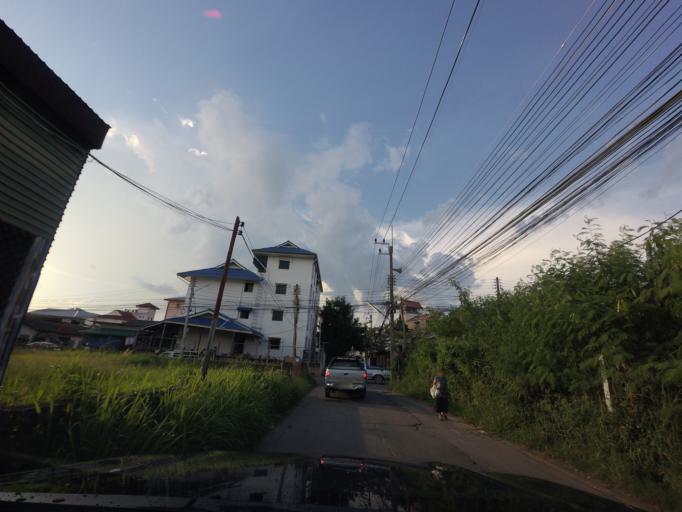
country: TH
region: Khon Kaen
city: Khon Kaen
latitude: 16.4250
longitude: 102.8613
